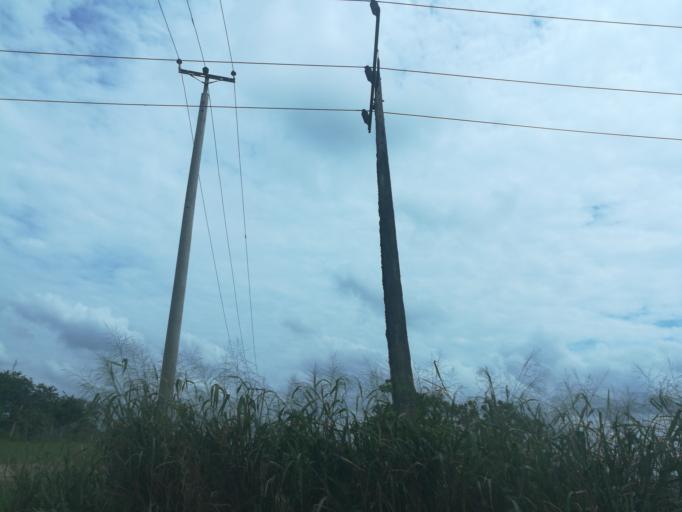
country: NG
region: Lagos
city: Ikotun
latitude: 6.4935
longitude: 3.1519
